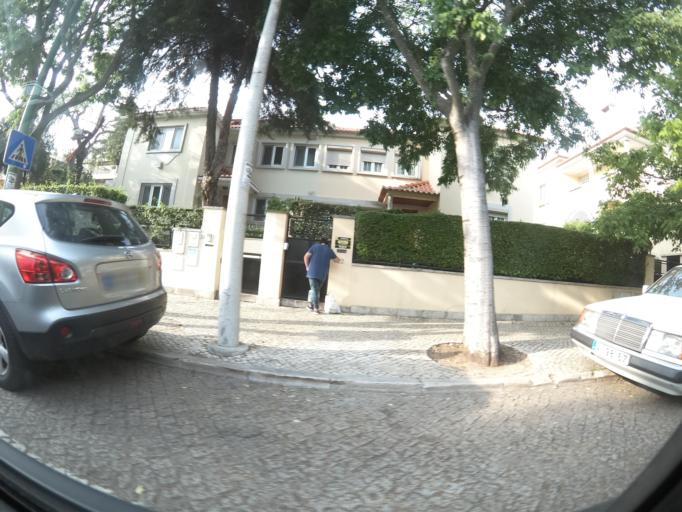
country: PT
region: Lisbon
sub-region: Oeiras
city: Alges
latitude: 38.6957
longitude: -9.2180
